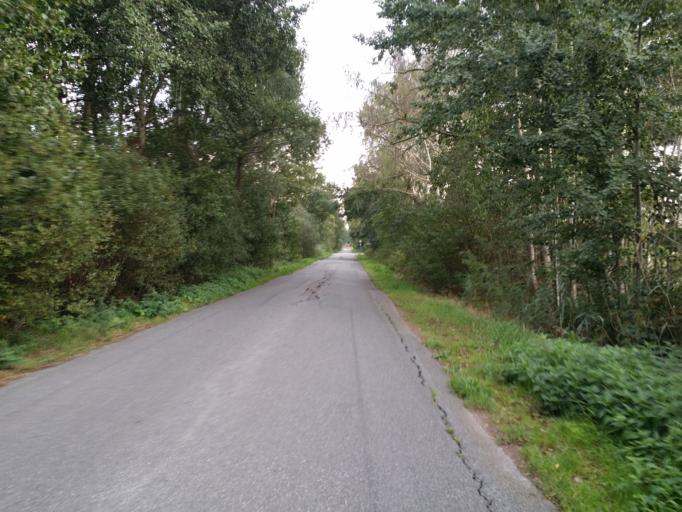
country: DE
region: Lower Saxony
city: Hollnseth
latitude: 53.5723
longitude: 9.1176
